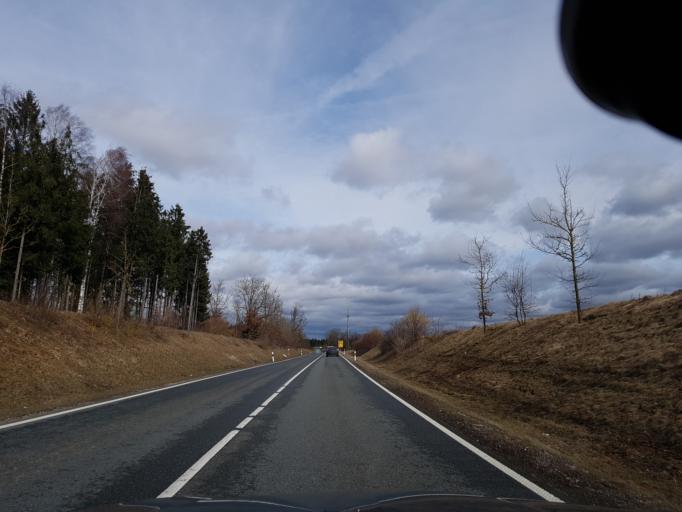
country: DE
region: Bavaria
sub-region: Upper Bavaria
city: Brunnthal
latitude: 48.0221
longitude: 11.6947
